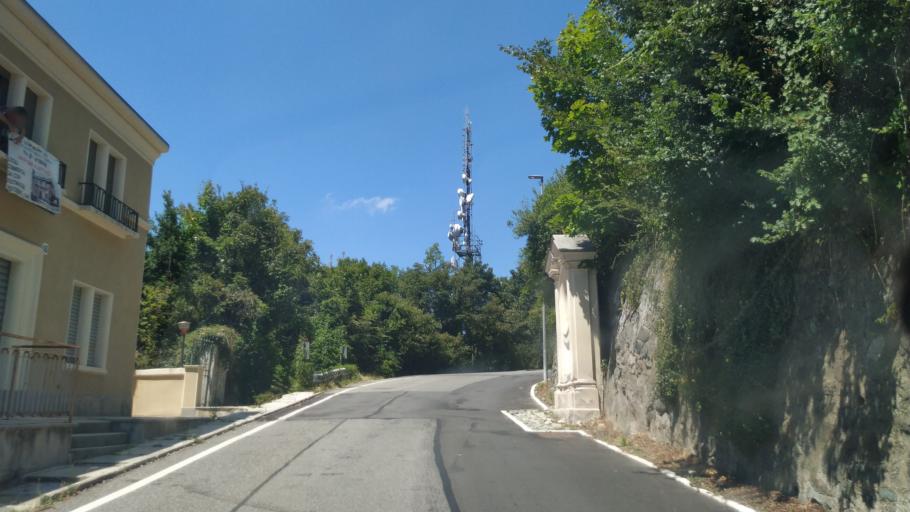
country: IT
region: Piedmont
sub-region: Provincia di Torino
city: San Mauro Torinese
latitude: 45.0794
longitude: 7.7666
